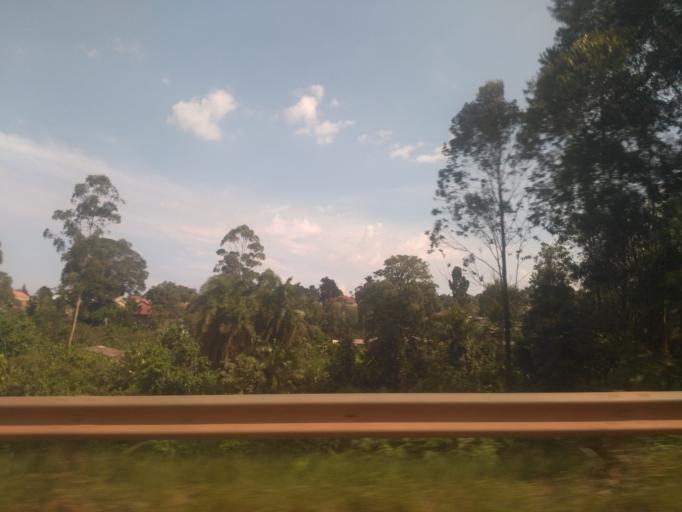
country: UG
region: Central Region
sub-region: Wakiso District
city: Kajansi
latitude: 0.2810
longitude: 32.4834
